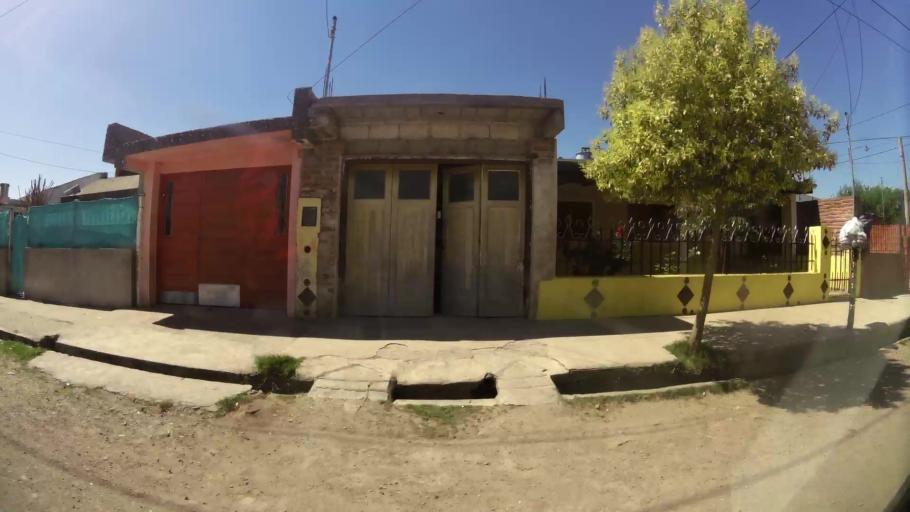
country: AR
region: Cordoba
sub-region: Departamento de Capital
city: Cordoba
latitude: -31.3668
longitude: -64.1417
